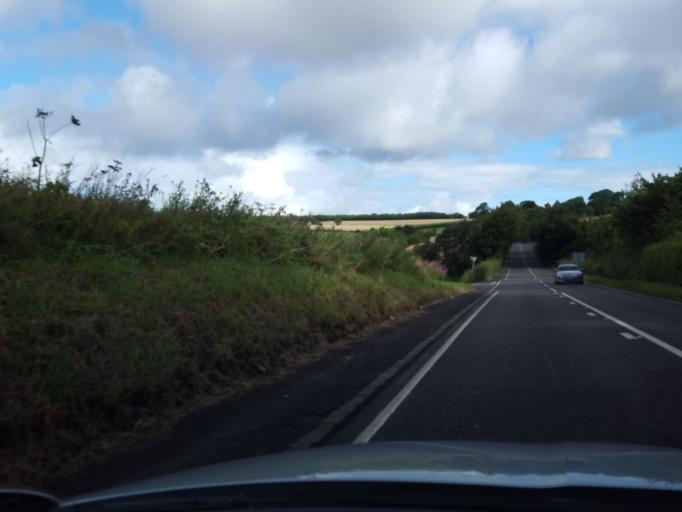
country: GB
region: Scotland
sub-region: West Lothian
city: Linlithgow
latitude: 55.9857
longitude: -3.6138
